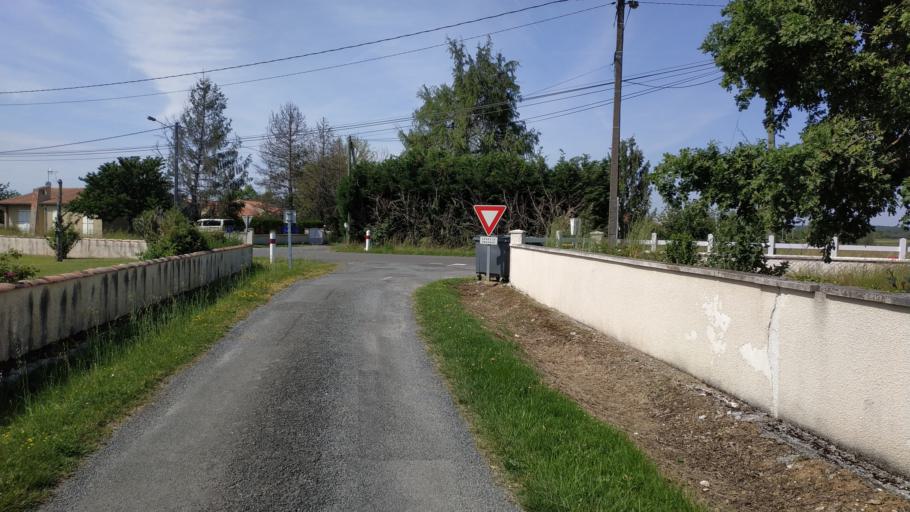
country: FR
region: Poitou-Charentes
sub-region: Departement de la Charente-Maritime
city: Saint-Germain-de-Lusignan
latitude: 45.4502
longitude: -0.4831
